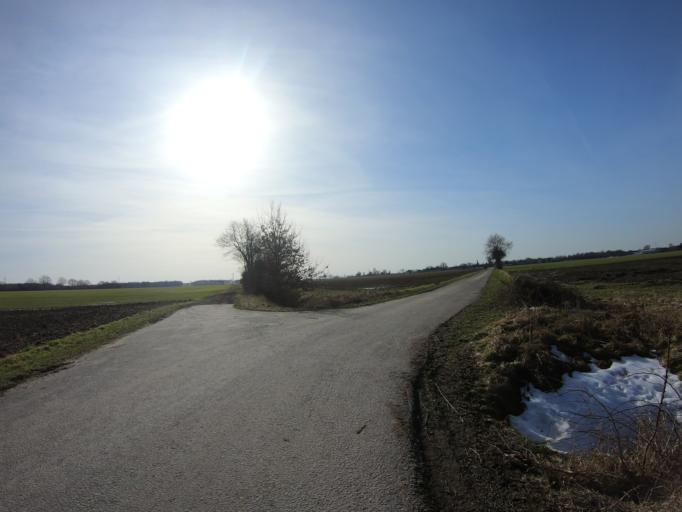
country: DE
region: Lower Saxony
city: Meine
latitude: 52.3901
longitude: 10.5563
